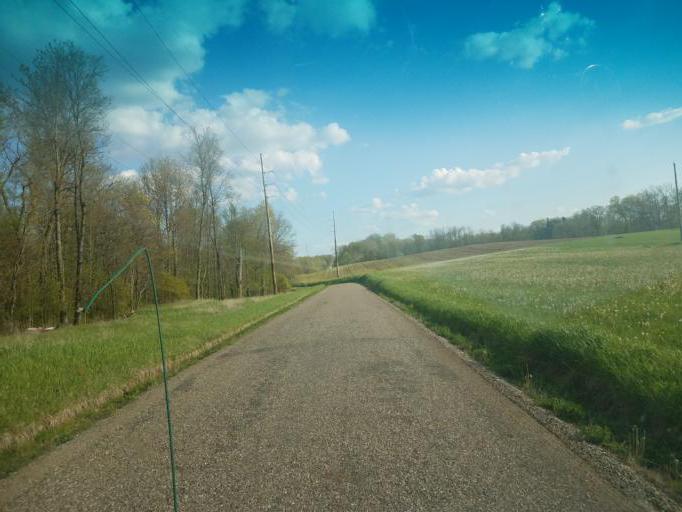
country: US
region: Ohio
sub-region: Wayne County
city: Shreve
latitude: 40.6623
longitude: -82.0339
